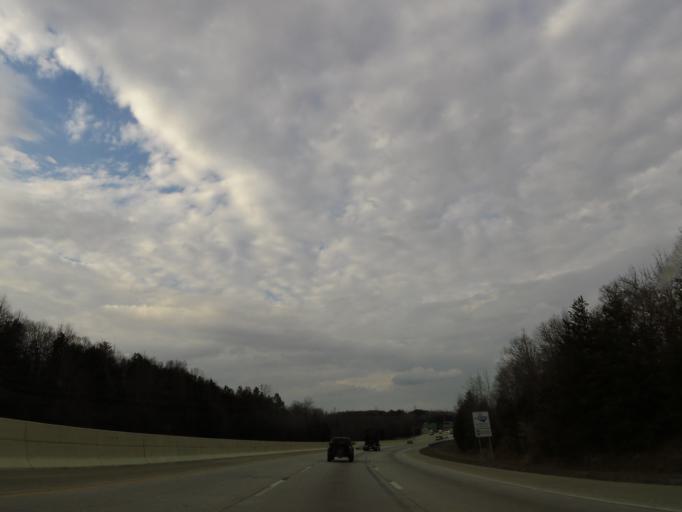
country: US
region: South Carolina
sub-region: Greenville County
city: Mauldin
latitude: 34.7848
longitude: -82.2811
